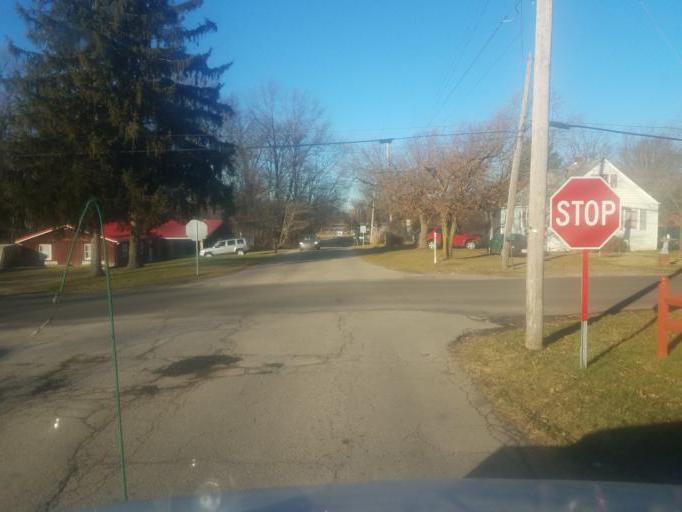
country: US
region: Ohio
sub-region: Richland County
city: Mansfield
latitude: 40.7872
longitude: -82.5509
